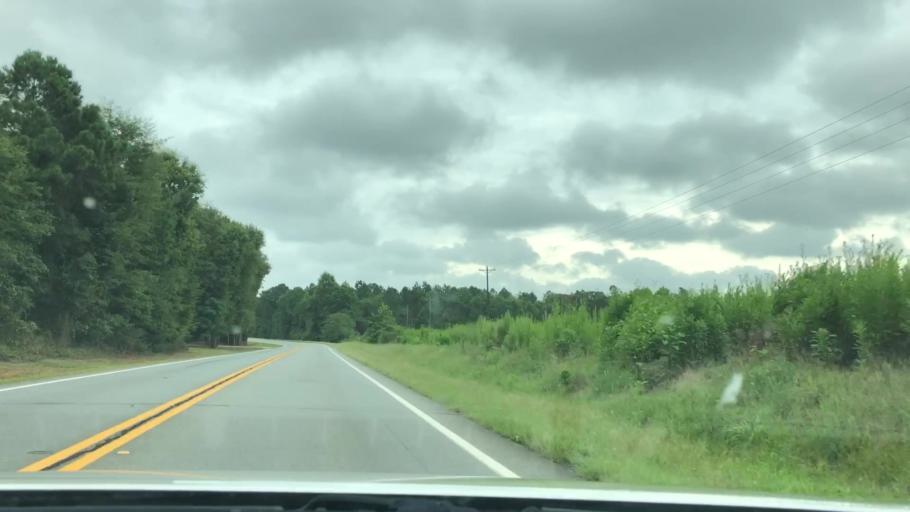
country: US
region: Georgia
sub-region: Pike County
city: Zebulon
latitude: 33.1054
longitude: -84.4120
